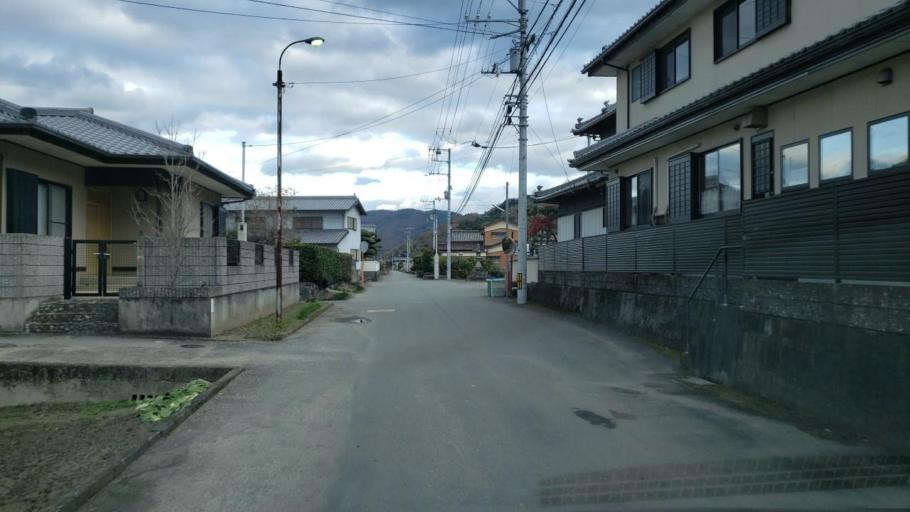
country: JP
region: Tokushima
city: Wakimachi
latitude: 34.0573
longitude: 134.1459
